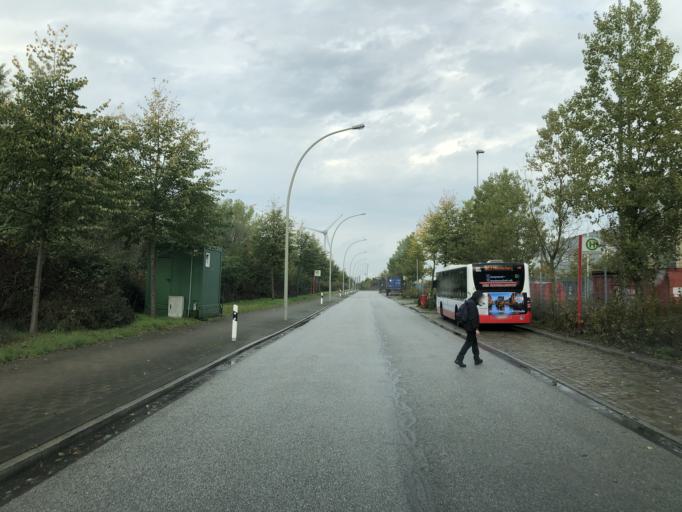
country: DE
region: Hamburg
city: Altona
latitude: 53.4982
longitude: 9.9192
